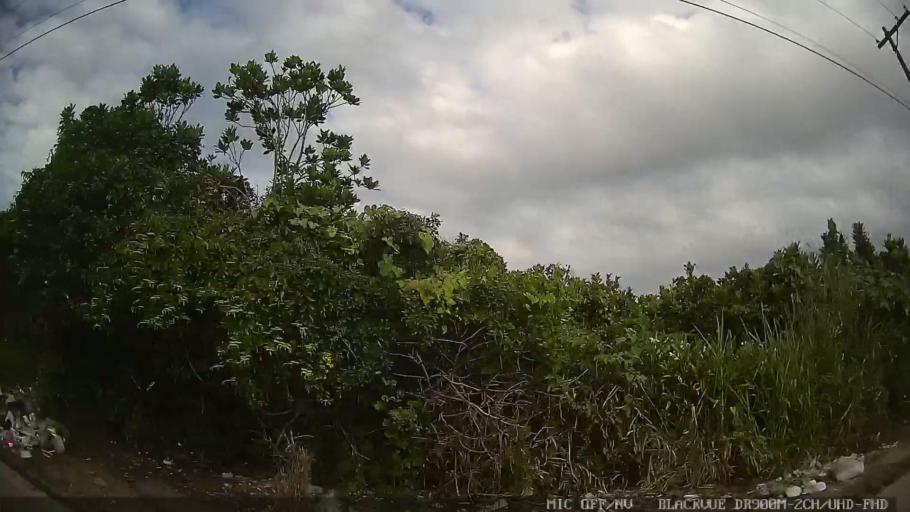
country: BR
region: Sao Paulo
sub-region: Itanhaem
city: Itanhaem
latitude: -24.1849
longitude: -46.8194
